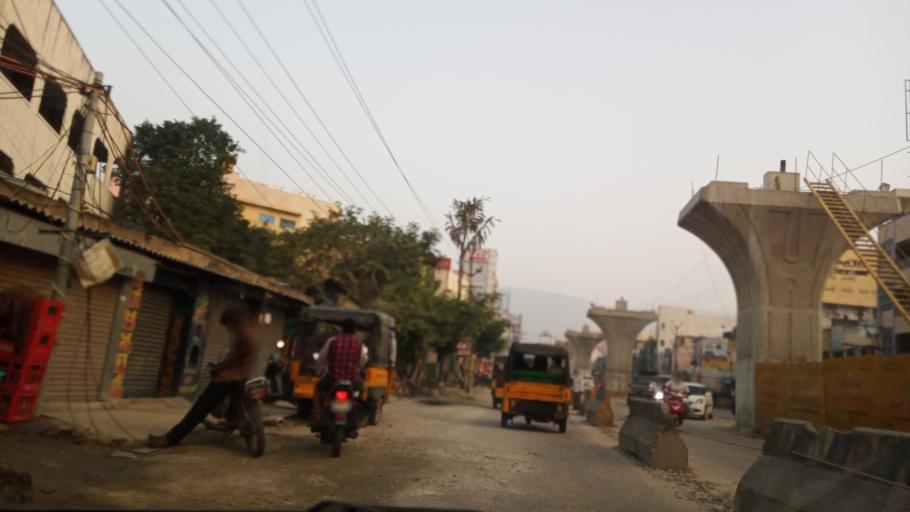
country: IN
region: Andhra Pradesh
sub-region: Chittoor
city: Tirupati
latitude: 13.6360
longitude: 79.4278
